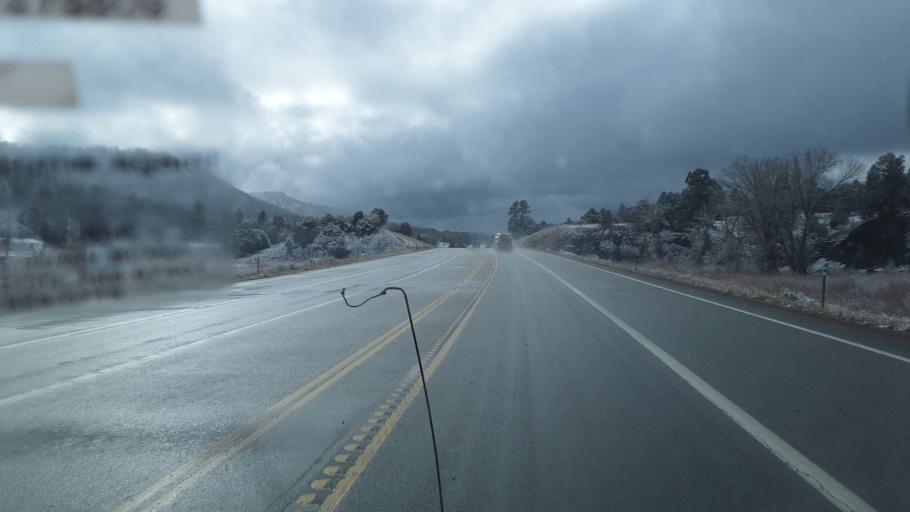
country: US
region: Colorado
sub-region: Archuleta County
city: Pagosa Springs
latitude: 37.2324
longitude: -107.1844
